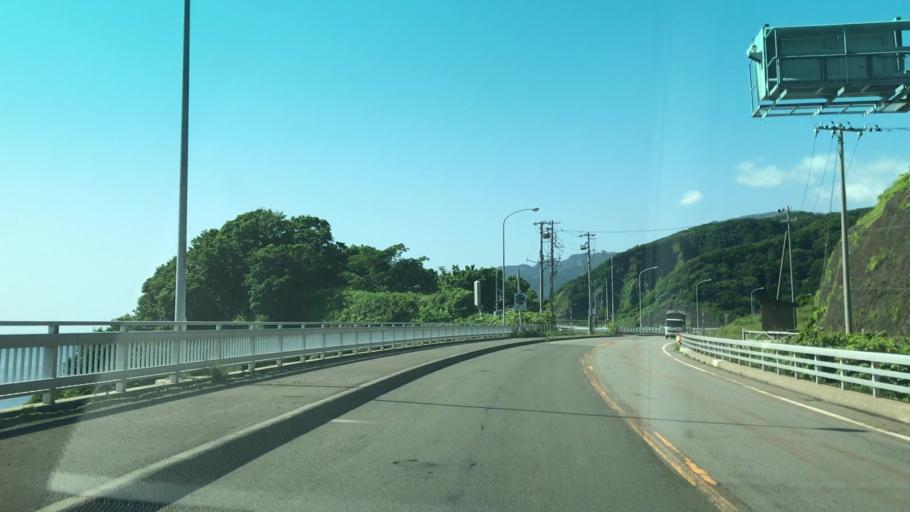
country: JP
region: Hokkaido
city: Iwanai
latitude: 43.1229
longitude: 140.4437
